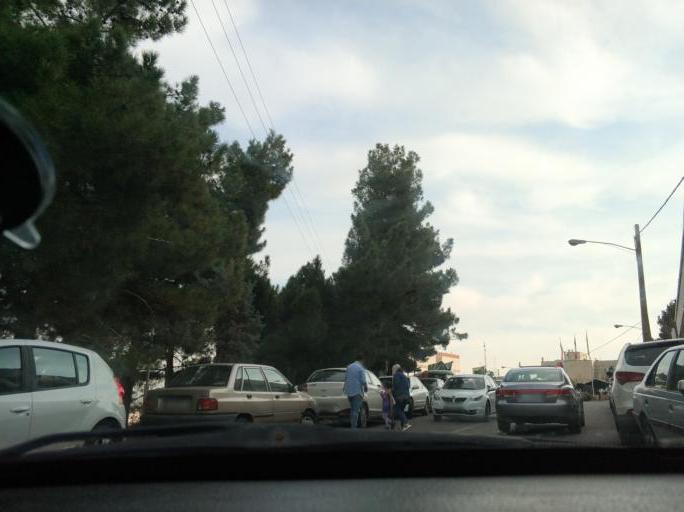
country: IR
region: Tehran
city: Tajrish
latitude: 35.8158
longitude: 51.4874
